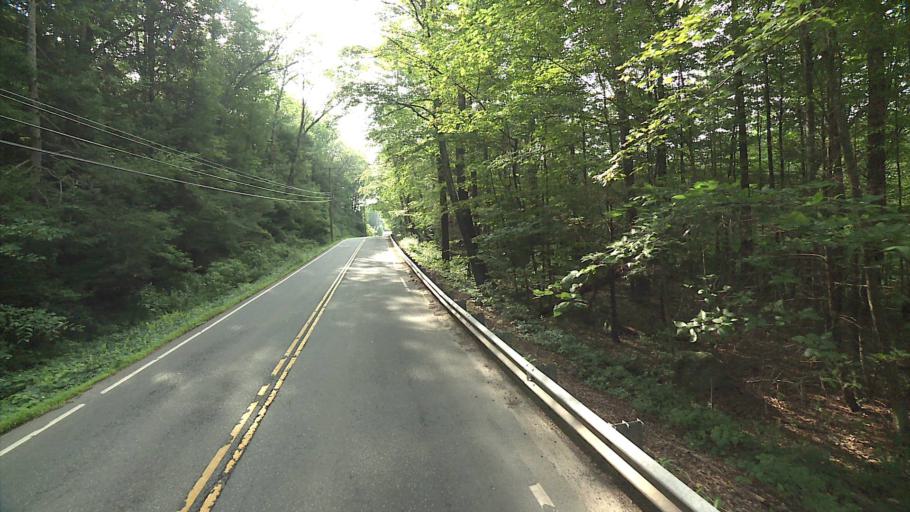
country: US
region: Massachusetts
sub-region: Worcester County
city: Southbridge
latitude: 41.9733
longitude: -72.0664
